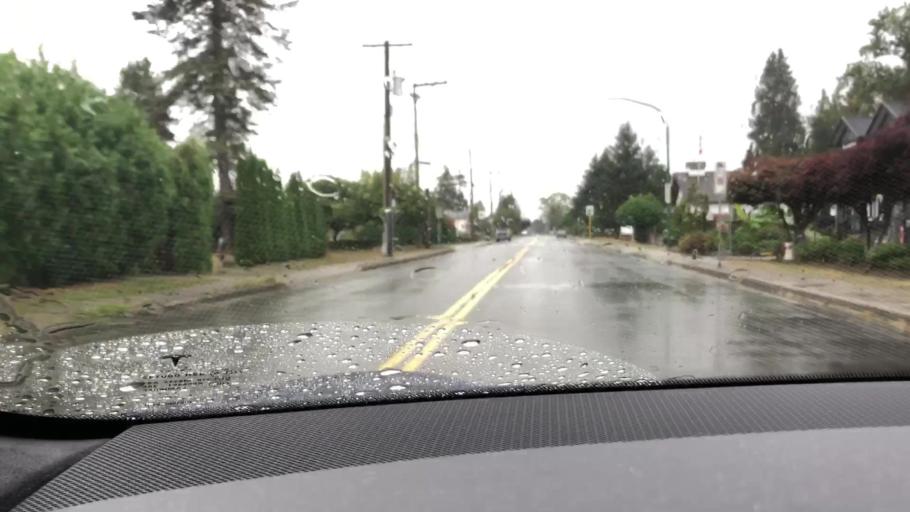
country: CA
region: British Columbia
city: New Westminster
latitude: 49.2319
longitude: -122.9113
